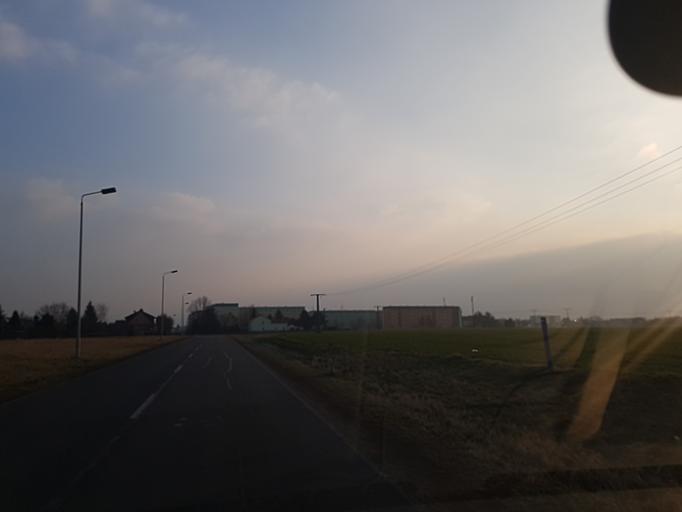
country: DE
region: Saxony-Anhalt
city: Coswig
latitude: 51.8968
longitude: 12.4593
